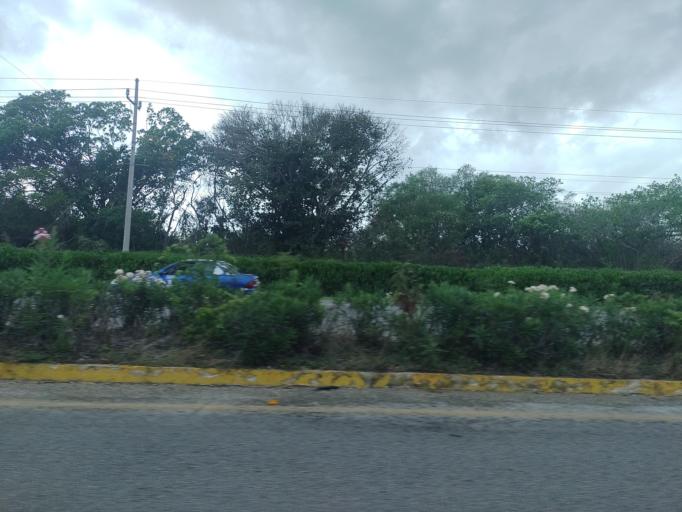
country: MX
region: Quintana Roo
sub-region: Tulum
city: Ciudad Chemuyil
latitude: 20.3808
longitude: -87.3298
